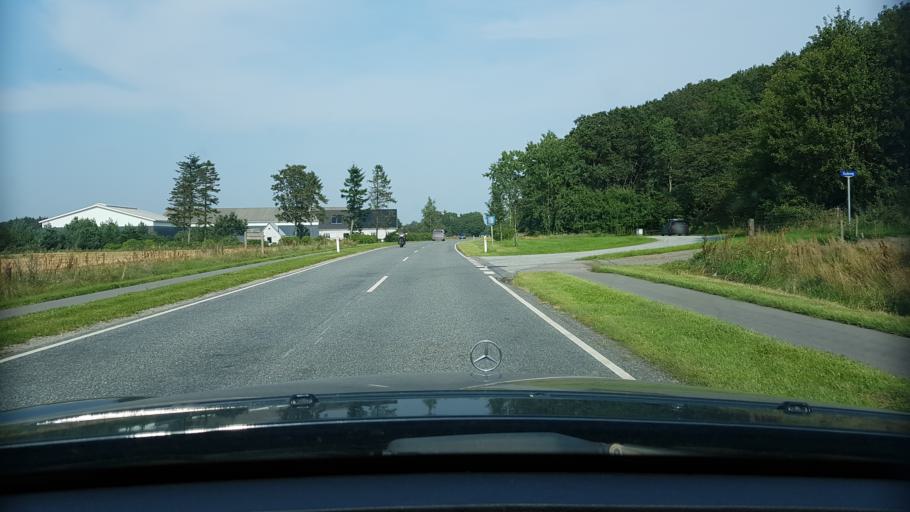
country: DK
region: North Denmark
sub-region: Alborg Kommune
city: Hals
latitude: 56.9127
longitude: 10.2538
